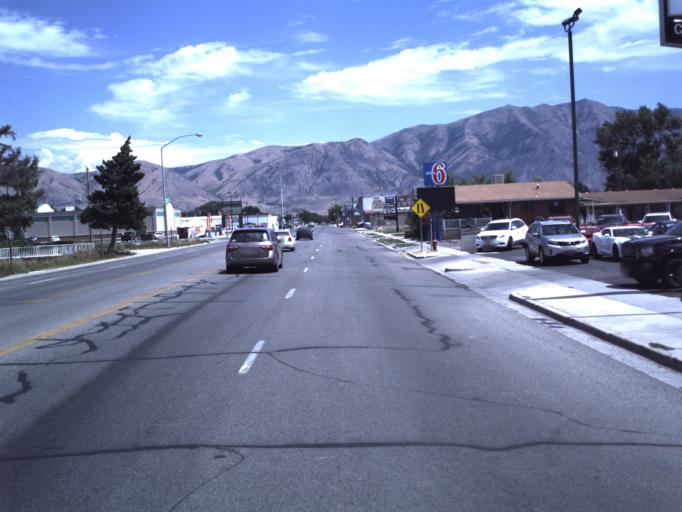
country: US
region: Utah
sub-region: Box Elder County
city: Tremonton
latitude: 41.7114
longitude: -112.1750
